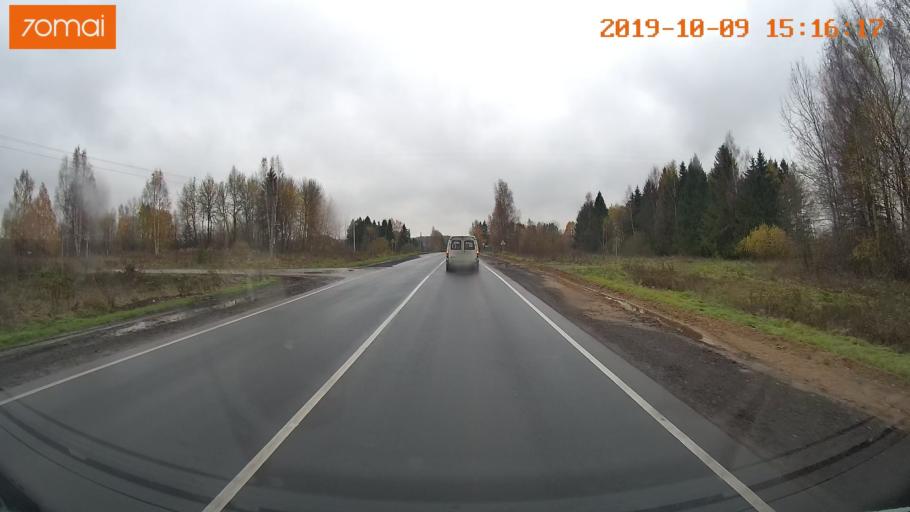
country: RU
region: Kostroma
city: Susanino
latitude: 58.1117
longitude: 41.5863
